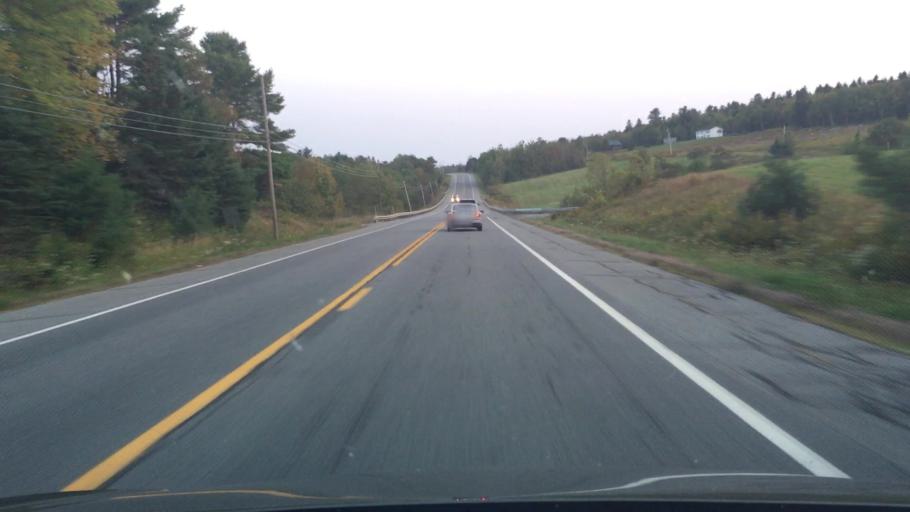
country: US
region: Maine
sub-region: Waldo County
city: Stockton Springs
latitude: 44.5304
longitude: -68.8614
